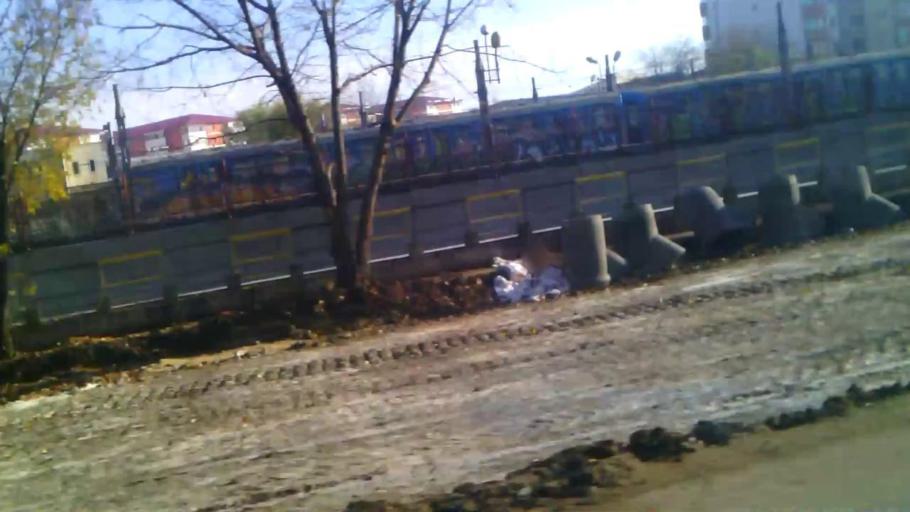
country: RO
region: Ilfov
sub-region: Comuna Popesti-Leordeni
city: Popesti-Leordeni
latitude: 44.3620
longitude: 26.1485
